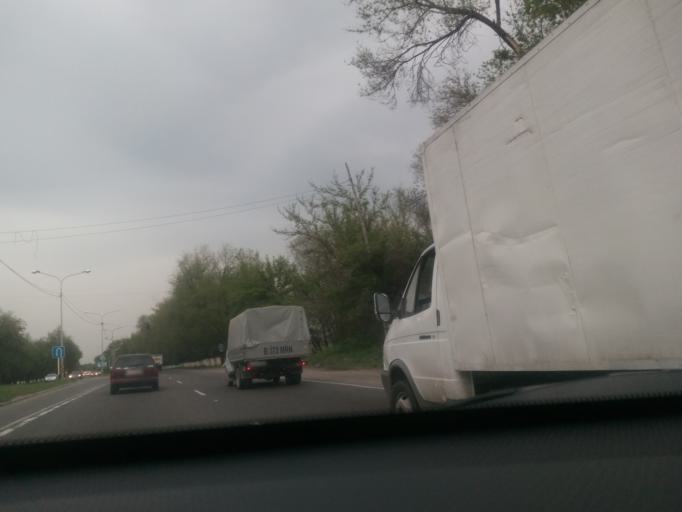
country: KZ
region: Almaty Oblysy
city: Burunday
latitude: 43.2172
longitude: 76.7034
